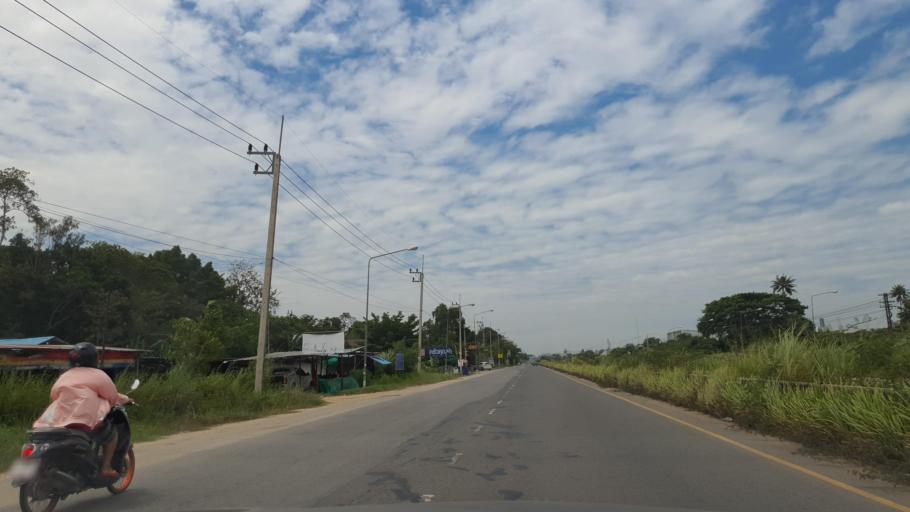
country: TH
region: Chon Buri
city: Phatthaya
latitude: 12.9711
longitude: 100.9248
